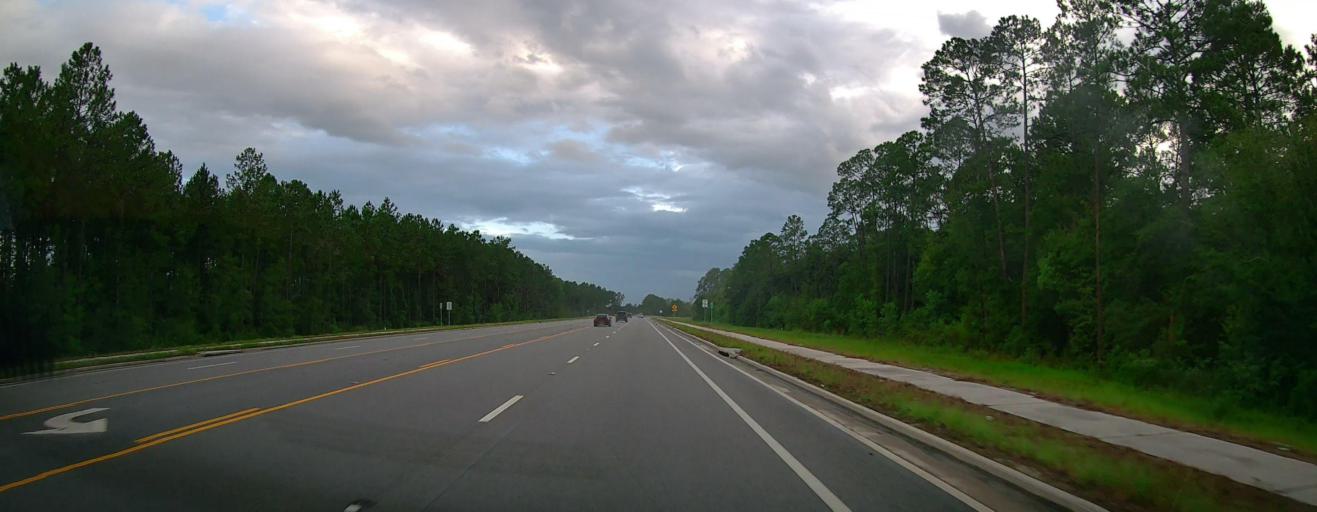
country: US
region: Georgia
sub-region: Ware County
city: Deenwood
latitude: 31.1889
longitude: -82.3882
